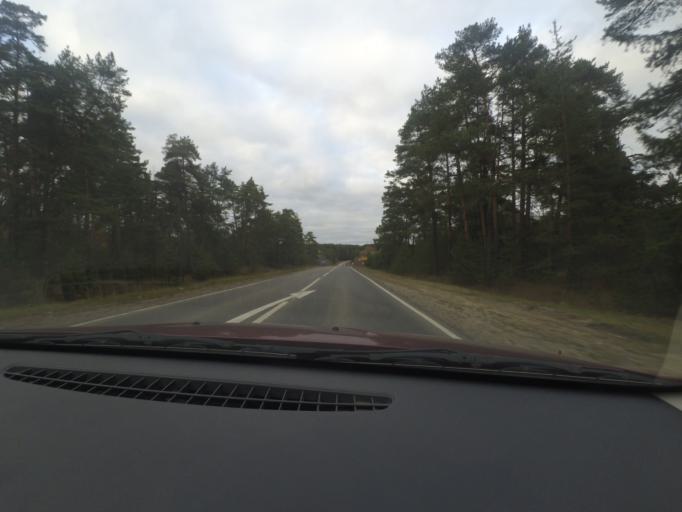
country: RU
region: Nizjnij Novgorod
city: Navashino
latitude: 55.6624
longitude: 42.2590
